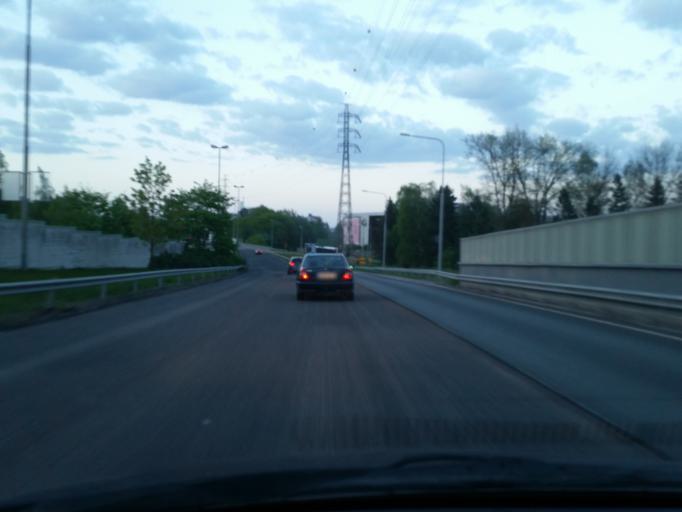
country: FI
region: Uusimaa
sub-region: Helsinki
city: Helsinki
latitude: 60.1889
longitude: 25.0130
